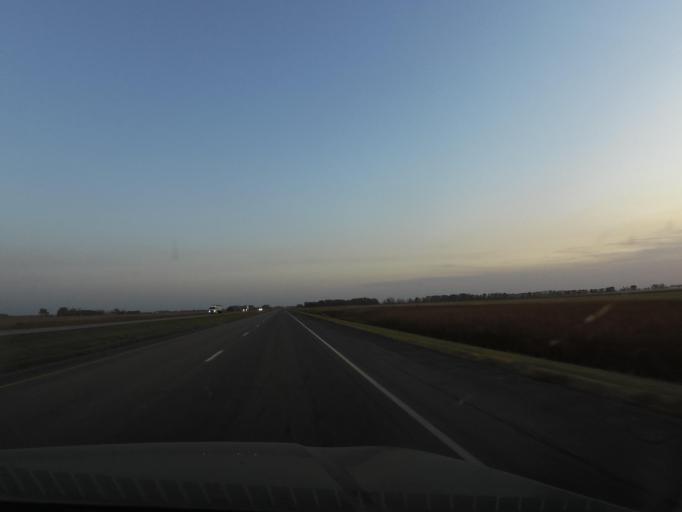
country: US
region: North Dakota
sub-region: Walsh County
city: Grafton
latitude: 48.5525
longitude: -97.1863
